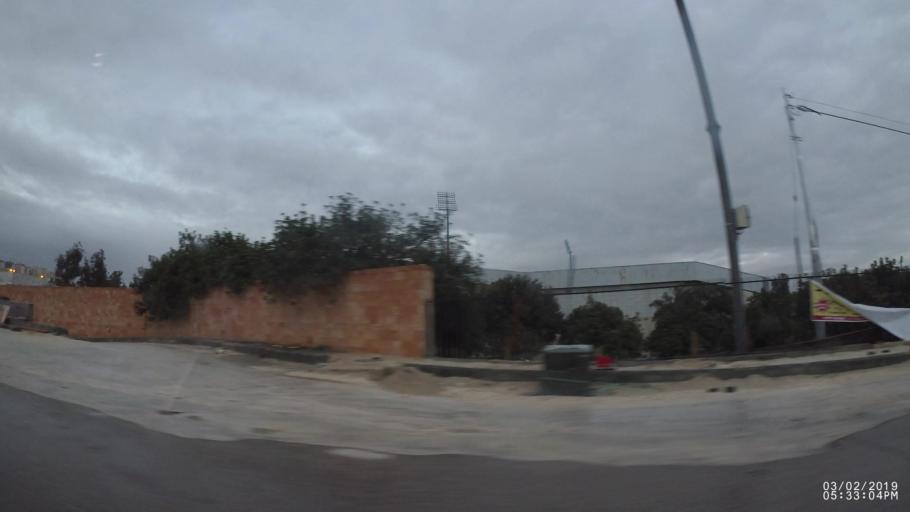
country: JO
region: Amman
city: Amman
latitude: 31.9834
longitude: 35.9008
